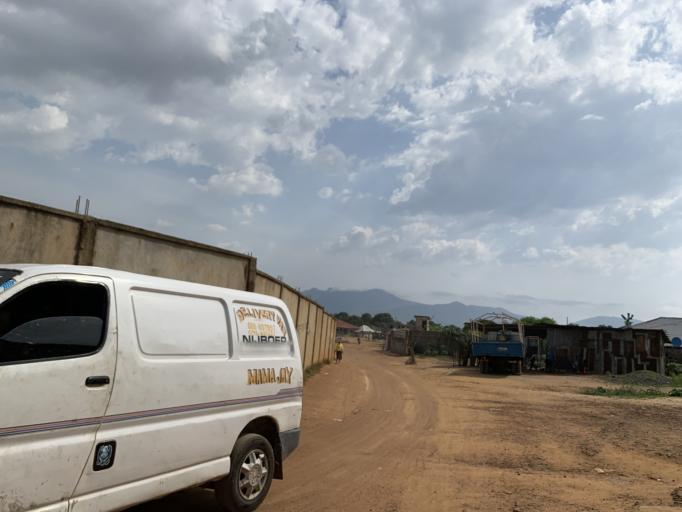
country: SL
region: Western Area
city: Waterloo
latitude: 8.3378
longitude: -13.0404
